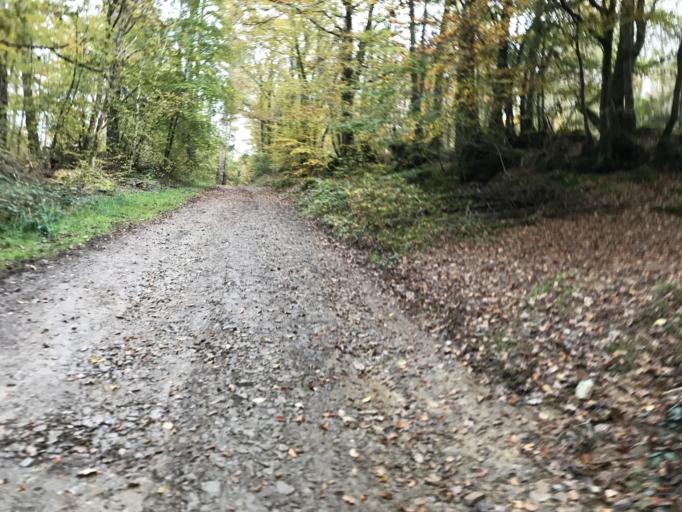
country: FR
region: Brittany
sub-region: Departement du Finistere
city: Irvillac
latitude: 48.3406
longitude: -4.2100
